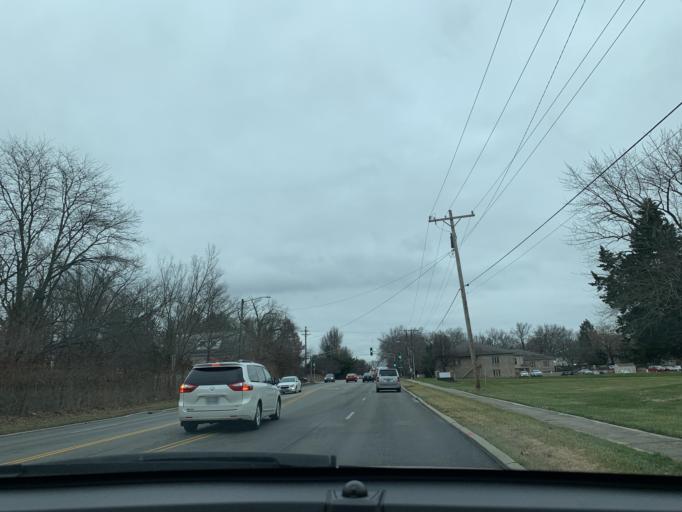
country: US
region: Illinois
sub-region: Sangamon County
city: Leland Grove
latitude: 39.7952
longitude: -89.6872
